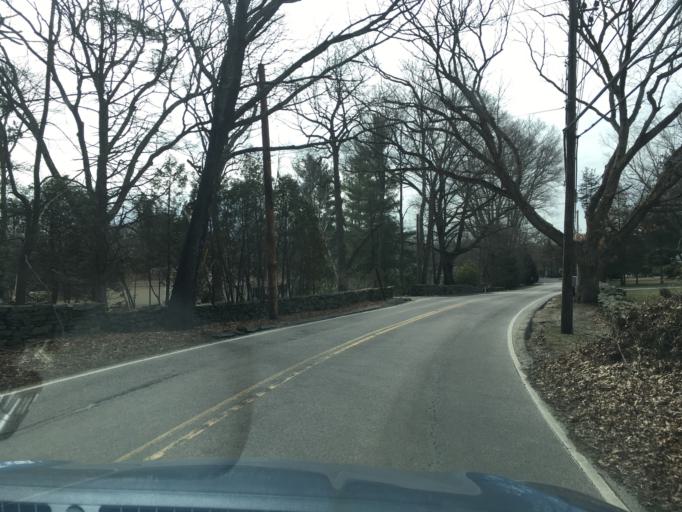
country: US
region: Rhode Island
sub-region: Kent County
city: East Greenwich
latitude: 41.6384
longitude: -71.4335
